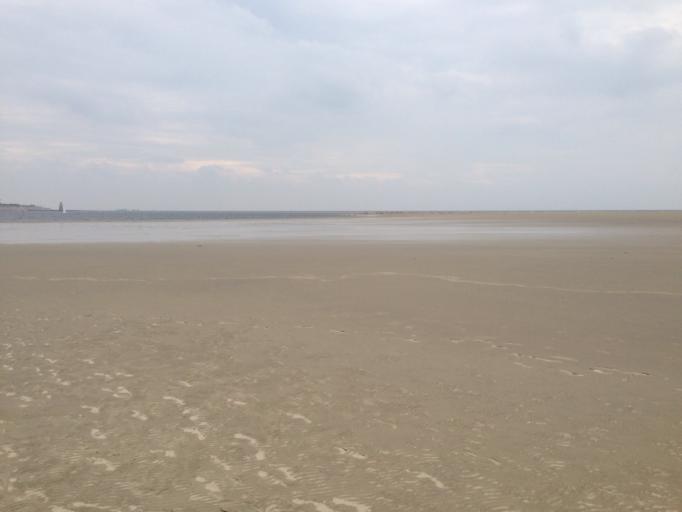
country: DE
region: Lower Saxony
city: Borkum
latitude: 53.5953
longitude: 6.6443
